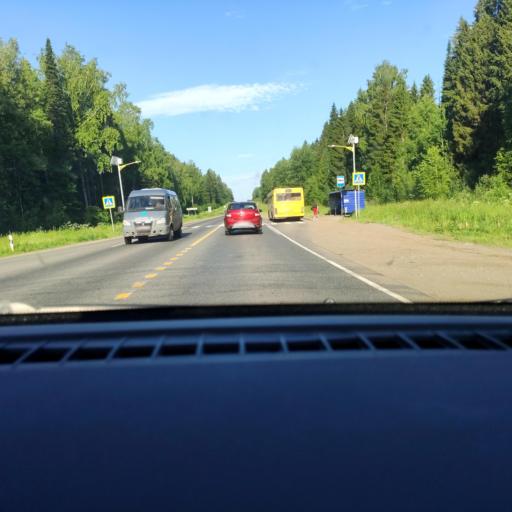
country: RU
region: Udmurtiya
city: Khokhryaki
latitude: 56.9162
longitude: 53.4393
